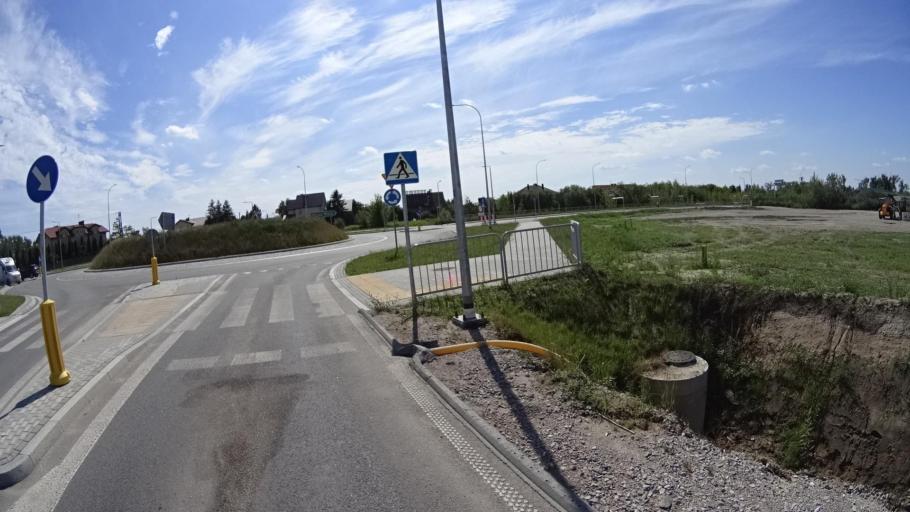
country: PL
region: Masovian Voivodeship
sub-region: Powiat piaseczynski
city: Mysiadlo
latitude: 52.1120
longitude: 20.9852
